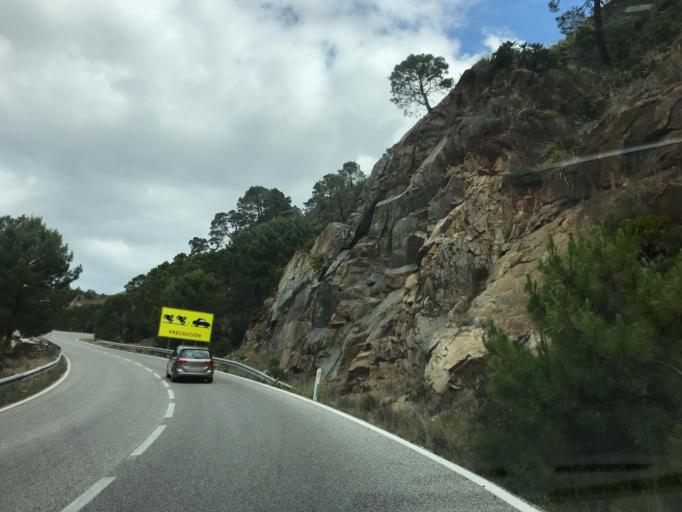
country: ES
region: Andalusia
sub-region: Provincia de Malaga
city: Benahavis
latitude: 36.5641
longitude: -5.0589
